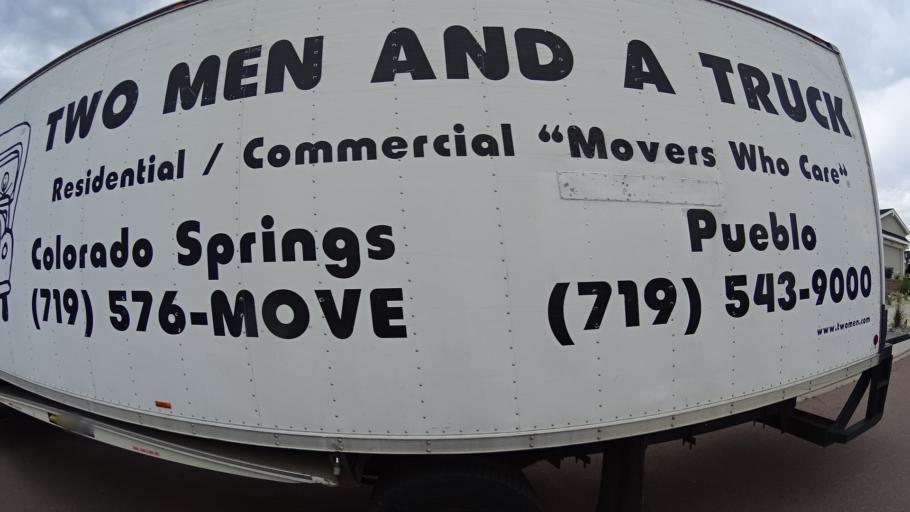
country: US
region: Colorado
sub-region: El Paso County
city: Gleneagle
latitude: 39.0043
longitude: -104.8057
